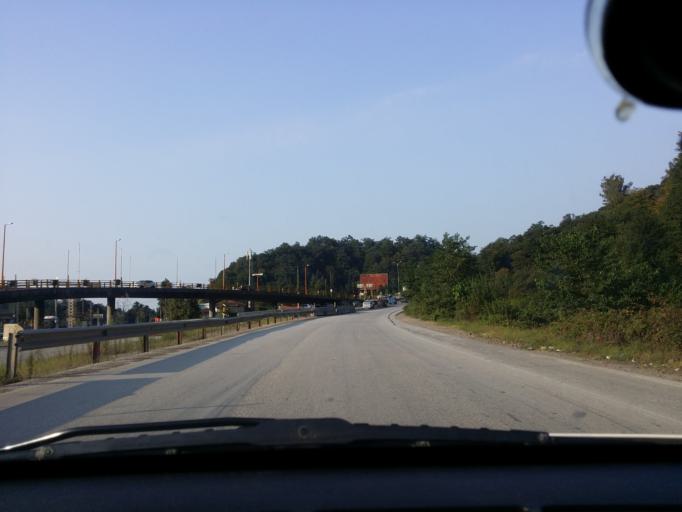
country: IR
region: Mazandaran
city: Chalus
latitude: 36.6343
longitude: 51.4101
